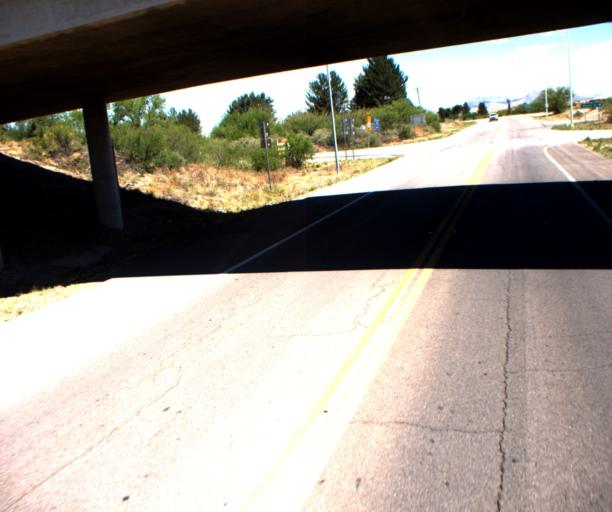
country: US
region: Arizona
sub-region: Cochise County
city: Benson
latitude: 31.9664
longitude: -110.2735
